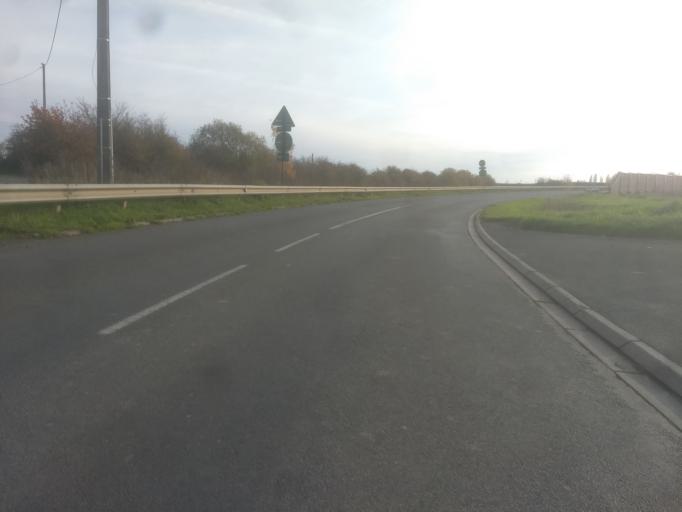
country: FR
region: Nord-Pas-de-Calais
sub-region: Departement du Pas-de-Calais
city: Agny
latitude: 50.2580
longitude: 2.7639
